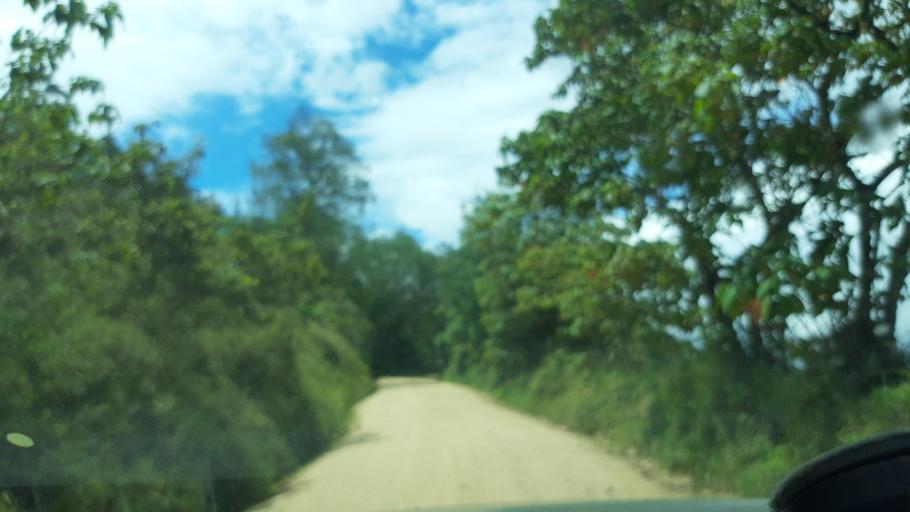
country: CO
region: Cundinamarca
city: Umbita
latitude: 5.2183
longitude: -73.4438
